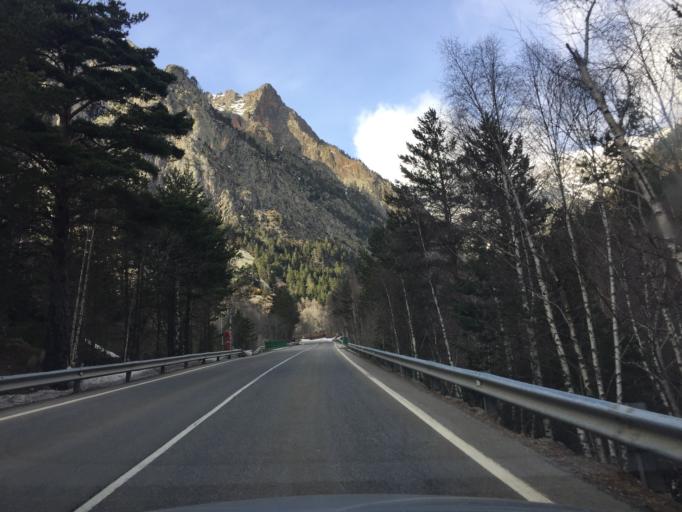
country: ES
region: Aragon
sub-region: Provincia de Huesca
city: Bielsa
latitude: 42.7008
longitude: 0.2015
